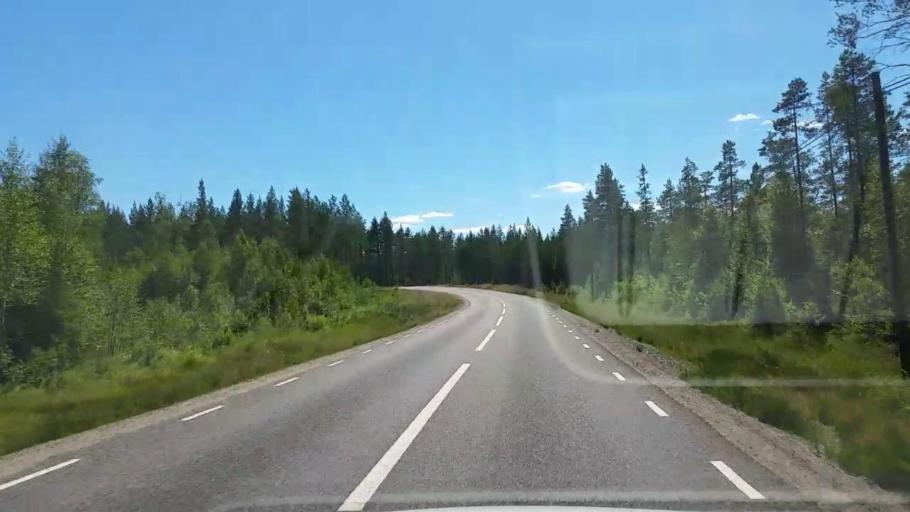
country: SE
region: Gaevleborg
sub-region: Ovanakers Kommun
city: Edsbyn
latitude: 61.4456
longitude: 15.7105
